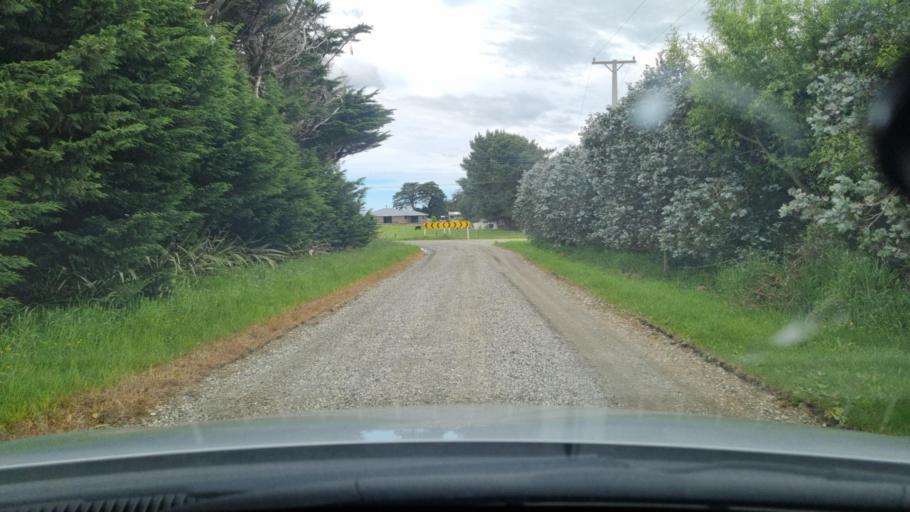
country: NZ
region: Southland
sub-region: Invercargill City
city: Invercargill
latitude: -46.4085
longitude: 168.2598
